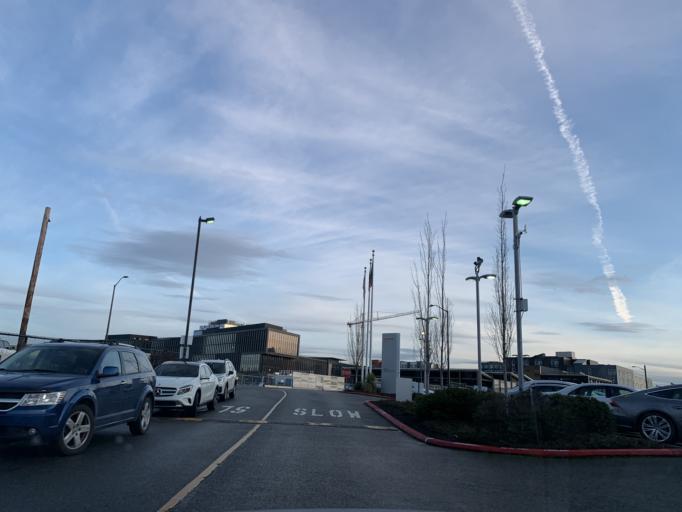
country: US
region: Washington
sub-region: King County
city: Bellevue
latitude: 47.6243
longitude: -122.1803
